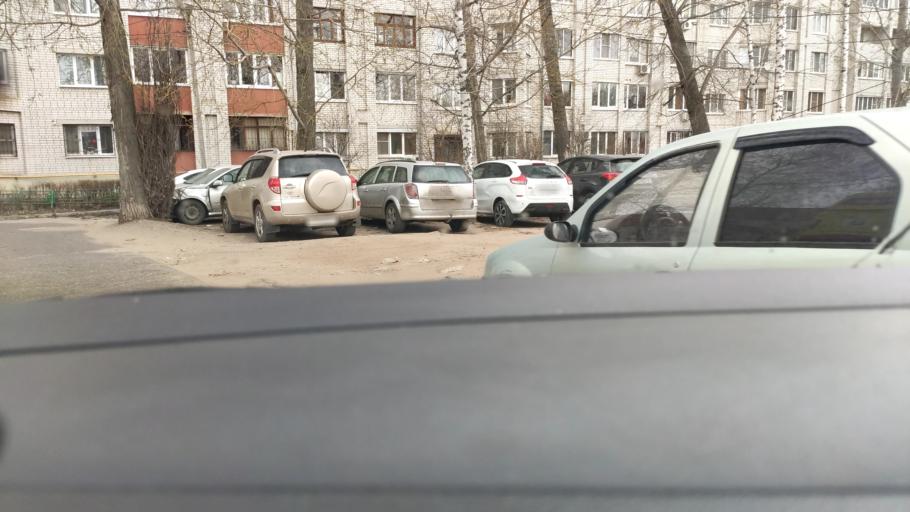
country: RU
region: Voronezj
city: Podgornoye
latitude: 51.7329
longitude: 39.1957
